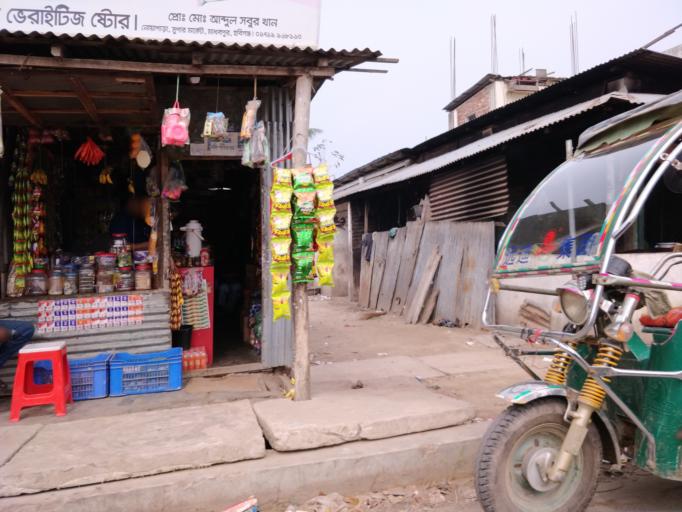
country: BD
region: Sylhet
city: Habiganj
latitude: 24.1724
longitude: 91.3555
